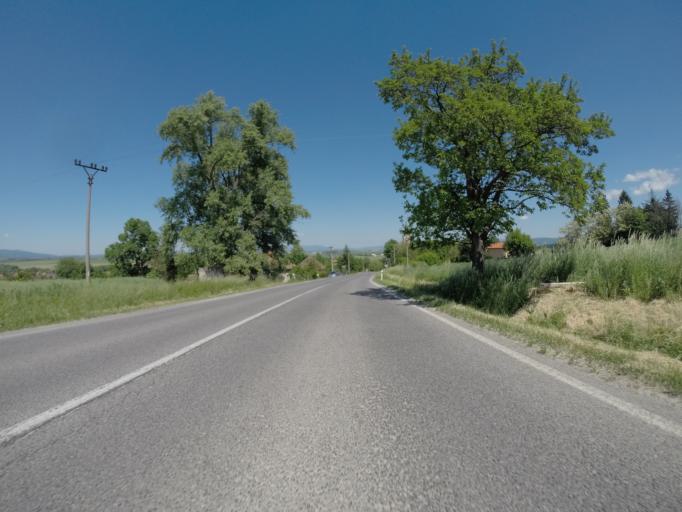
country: SK
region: Nitriansky
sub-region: Okres Nitra
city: Nitra
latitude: 48.5304
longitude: 18.0927
